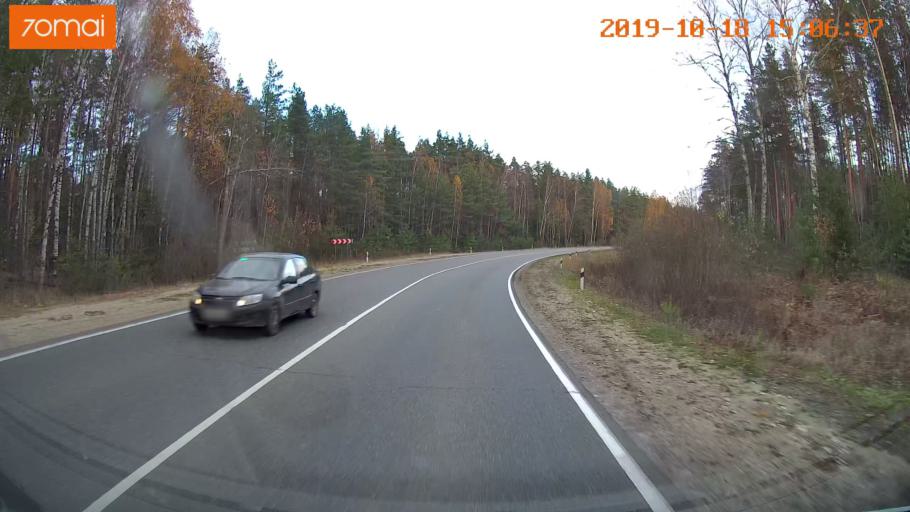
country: RU
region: Vladimir
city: Gus'-Khrustal'nyy
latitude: 55.5327
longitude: 40.5800
